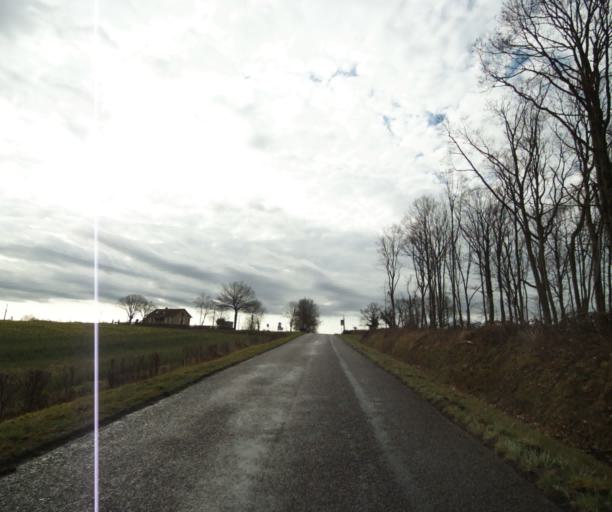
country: FR
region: Auvergne
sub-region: Departement de l'Allier
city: Toulon-sur-Allier
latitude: 46.5303
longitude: 3.4075
